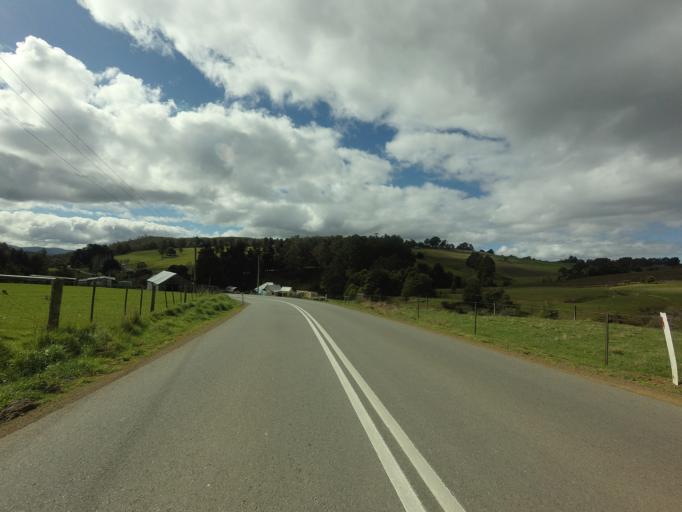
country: AU
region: Tasmania
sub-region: Huon Valley
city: Geeveston
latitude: -43.2425
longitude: 146.9919
